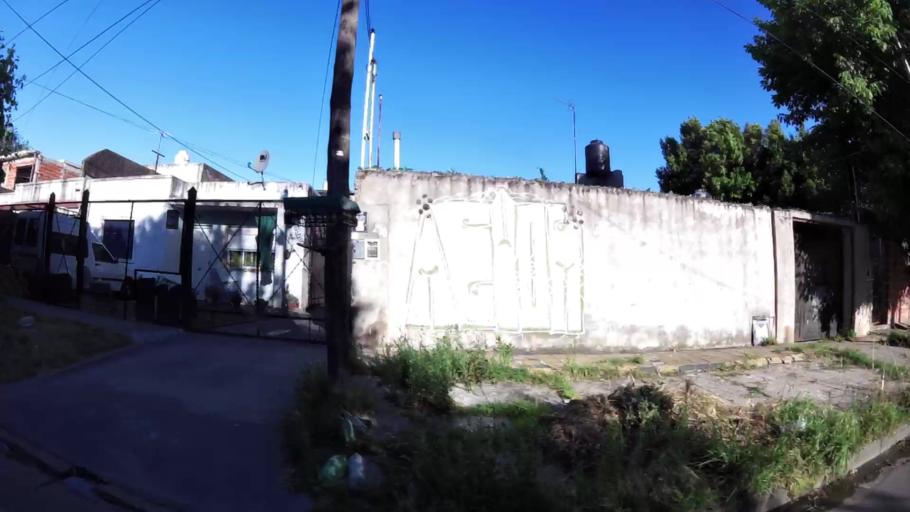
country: AR
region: Buenos Aires
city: Ituzaingo
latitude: -34.6905
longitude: -58.6429
